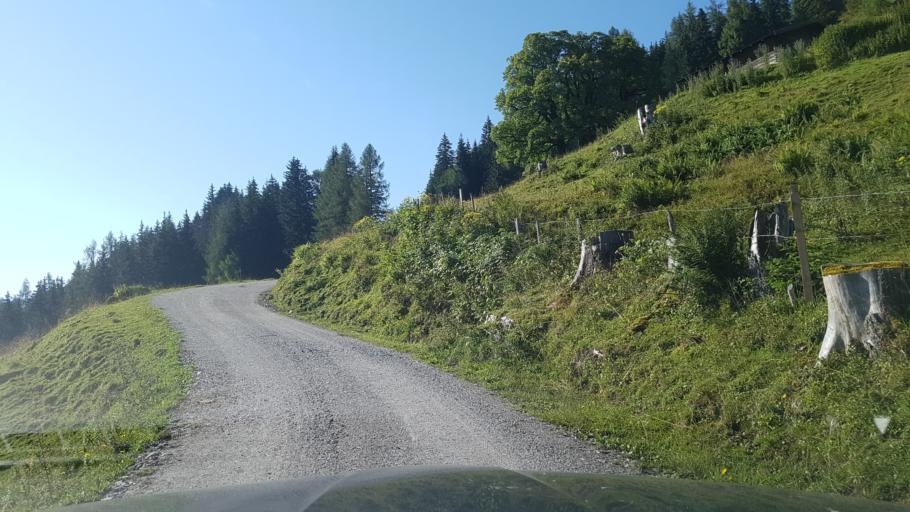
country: AT
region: Salzburg
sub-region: Politischer Bezirk Sankt Johann im Pongau
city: Dorfgastein
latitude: 47.2495
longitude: 13.0730
